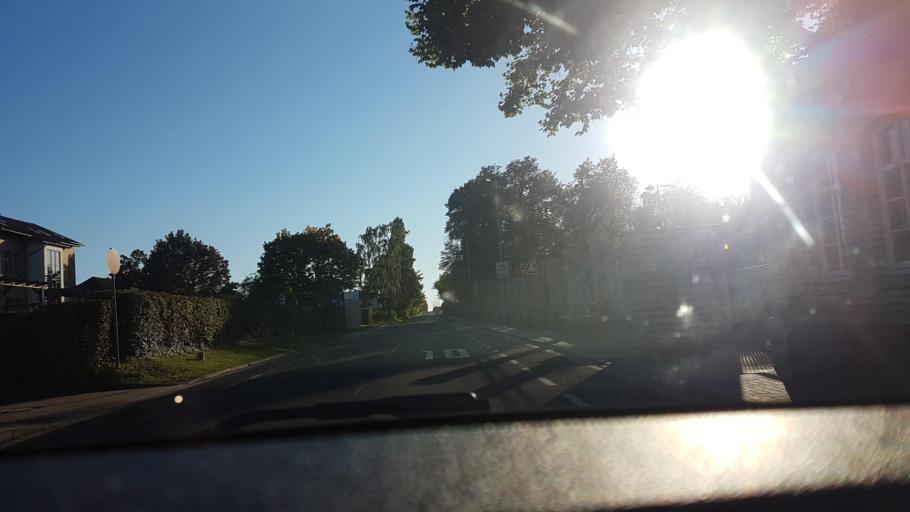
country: DE
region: Saxony-Anhalt
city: Bernburg
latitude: 51.7865
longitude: 11.7297
